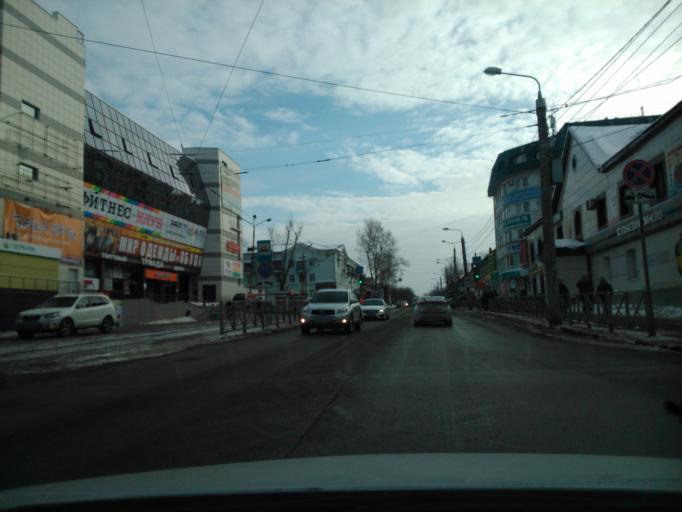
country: RU
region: Perm
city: Perm
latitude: 57.9988
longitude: 56.2423
